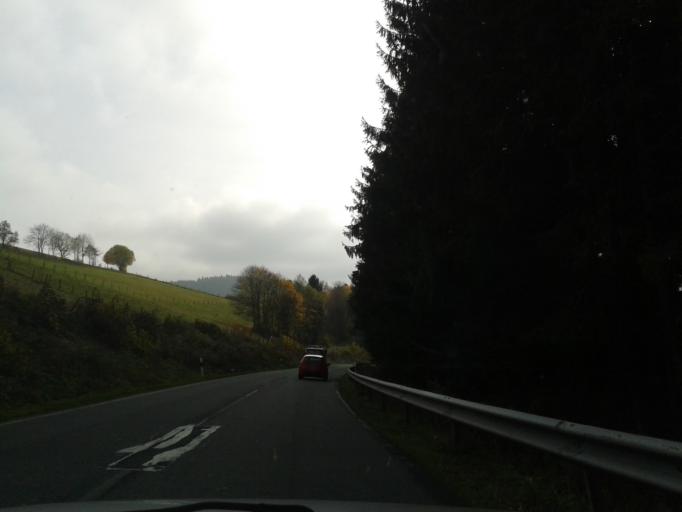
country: DE
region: North Rhine-Westphalia
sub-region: Regierungsbezirk Arnsberg
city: Bad Berleburg
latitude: 51.1082
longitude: 8.4324
